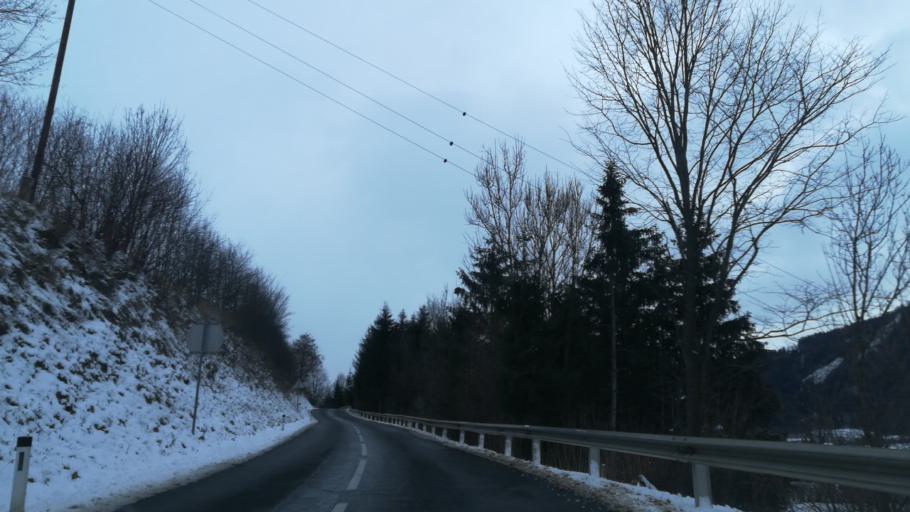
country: AT
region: Styria
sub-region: Politischer Bezirk Murtal
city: Sankt Georgen ob Judenburg
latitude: 47.2104
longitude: 14.5174
